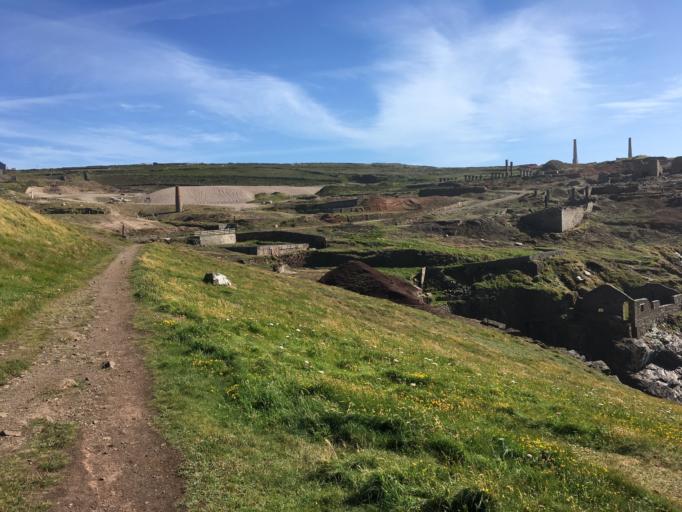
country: GB
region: England
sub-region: Cornwall
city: Saint Just
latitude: 50.1567
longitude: -5.6798
